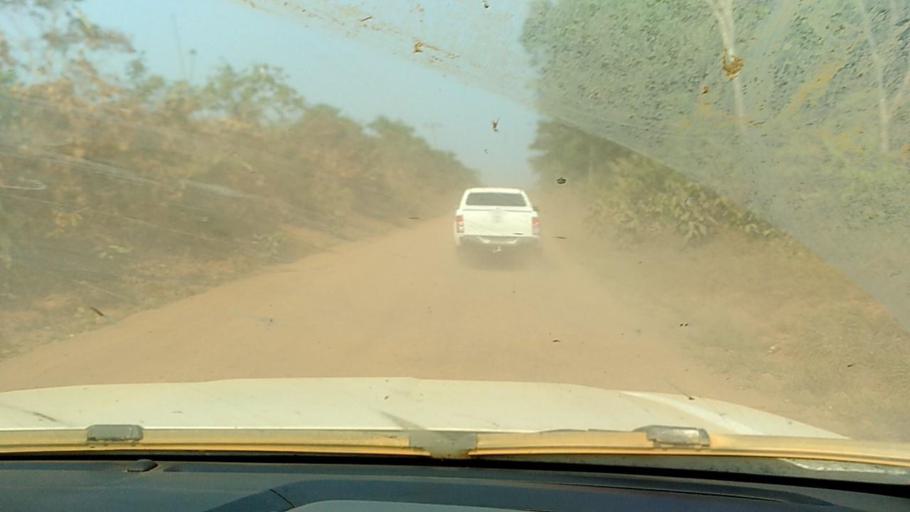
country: BR
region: Rondonia
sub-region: Porto Velho
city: Porto Velho
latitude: -8.8415
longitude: -64.1559
